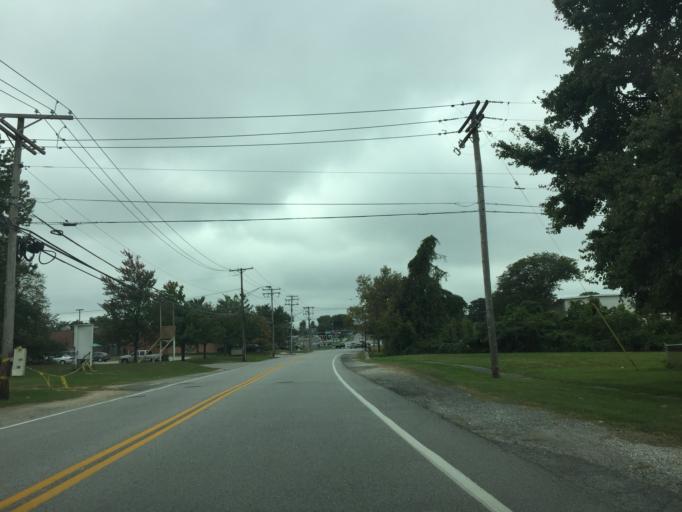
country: US
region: Maryland
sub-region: Baltimore County
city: Middle River
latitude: 39.3378
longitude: -76.4560
